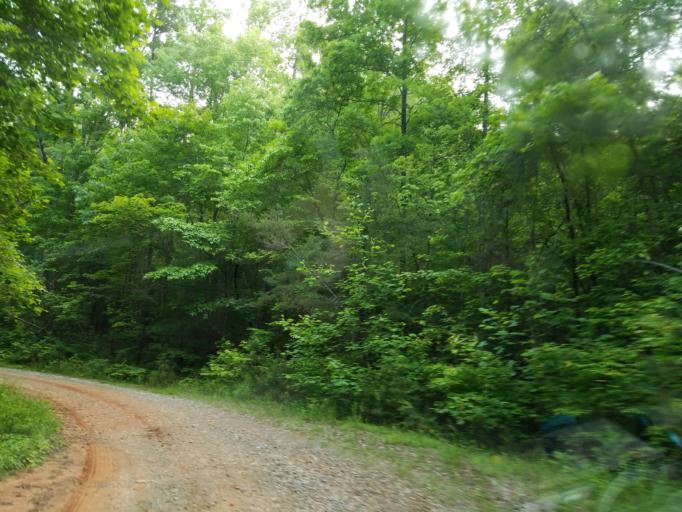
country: US
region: Georgia
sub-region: Dawson County
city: Dawsonville
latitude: 34.5808
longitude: -84.1464
